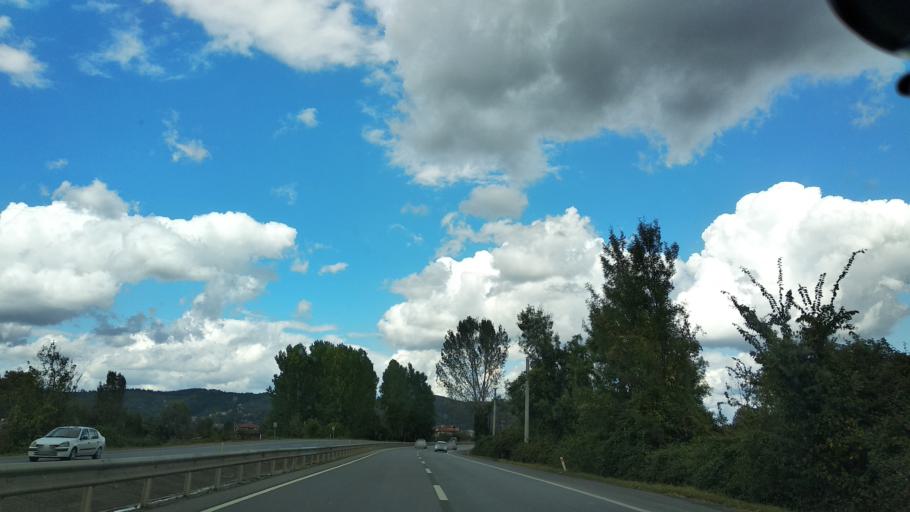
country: TR
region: Sakarya
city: Adapazari
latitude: 40.8015
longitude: 30.4316
